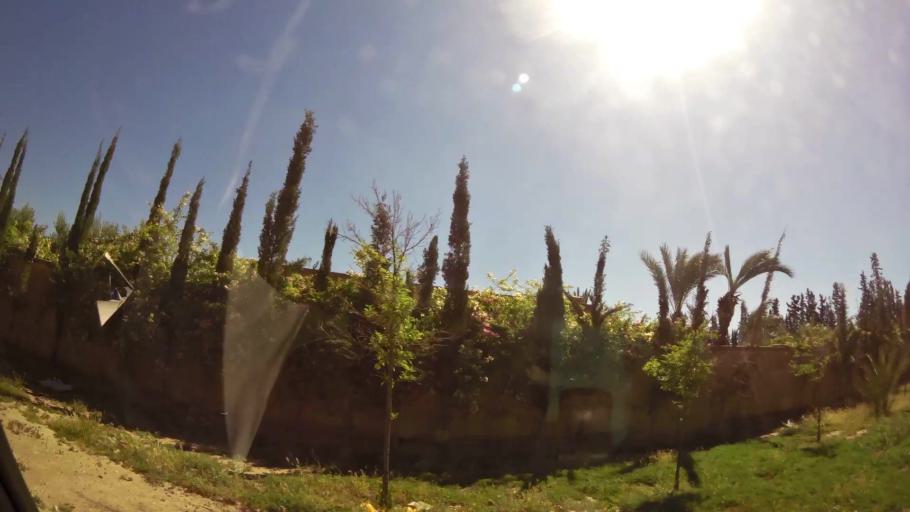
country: MA
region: Marrakech-Tensift-Al Haouz
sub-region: Marrakech
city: Marrakesh
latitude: 31.6692
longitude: -7.9600
